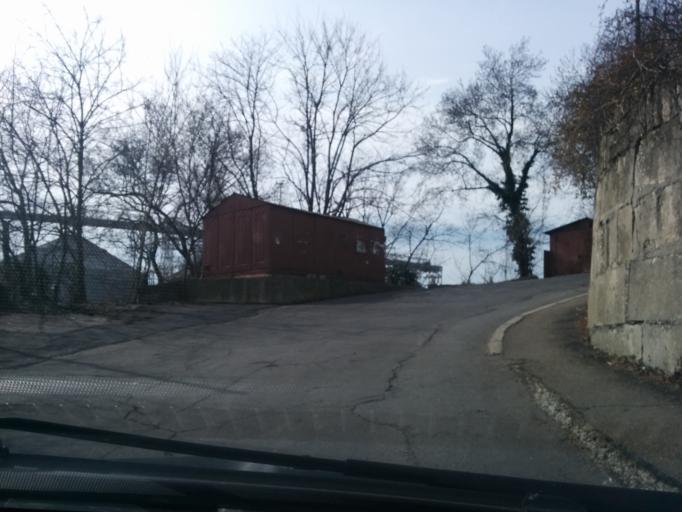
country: RU
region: Krasnodarskiy
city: Tuapse
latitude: 44.0971
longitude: 39.0679
